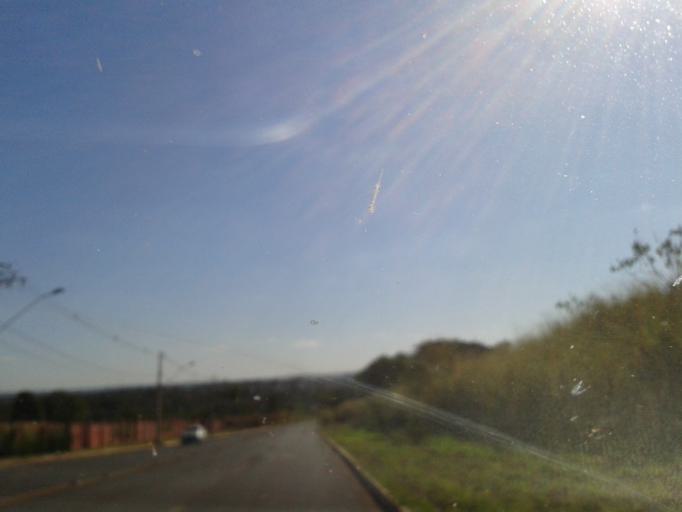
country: BR
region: Goias
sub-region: Itumbiara
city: Itumbiara
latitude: -18.4273
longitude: -49.2002
